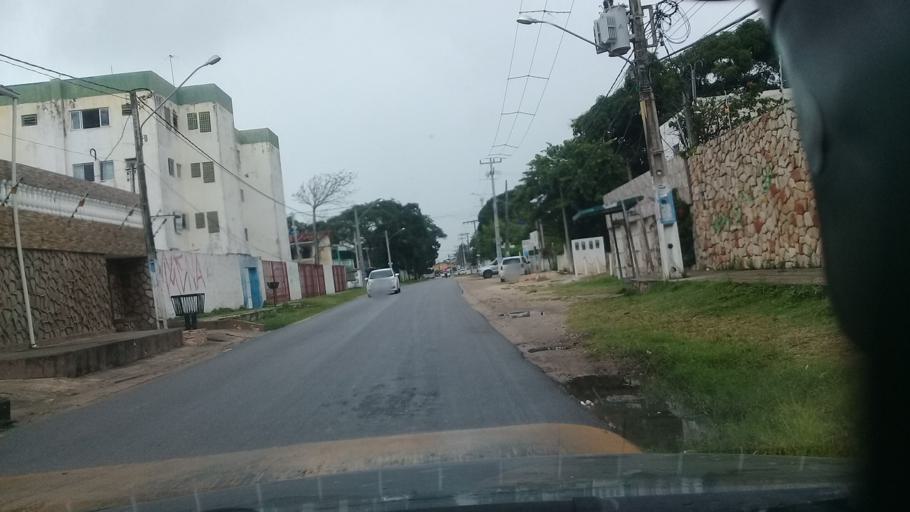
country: BR
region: Pernambuco
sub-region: Itamaraca
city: Itamaraca
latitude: -7.7380
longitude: -34.8251
